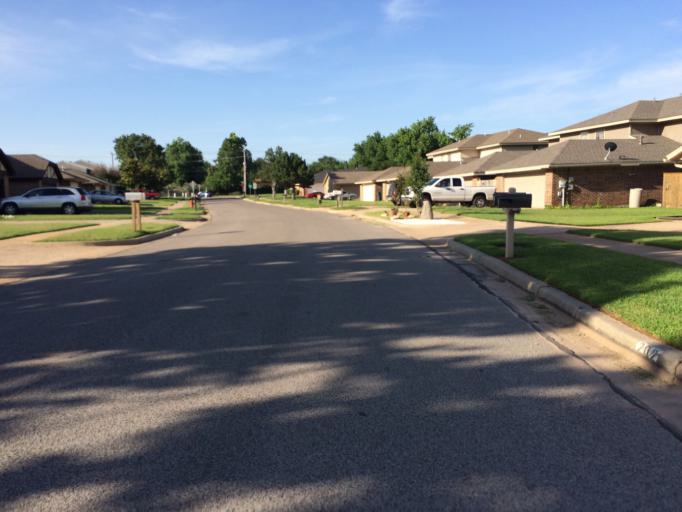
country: US
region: Oklahoma
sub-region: Cleveland County
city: Norman
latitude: 35.2198
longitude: -97.5004
